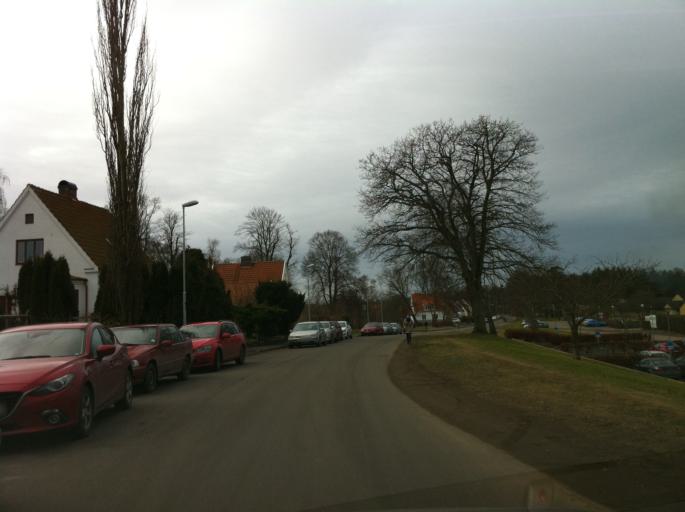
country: SE
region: Skane
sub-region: Angelholms Kommun
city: AEngelholm
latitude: 56.2395
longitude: 12.8563
